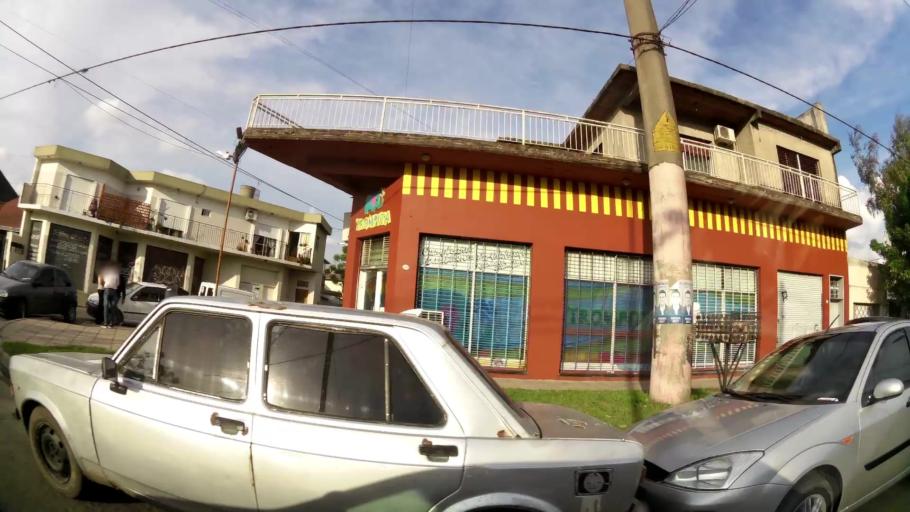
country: AR
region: Buenos Aires
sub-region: Partido de Quilmes
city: Quilmes
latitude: -34.7406
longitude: -58.2691
